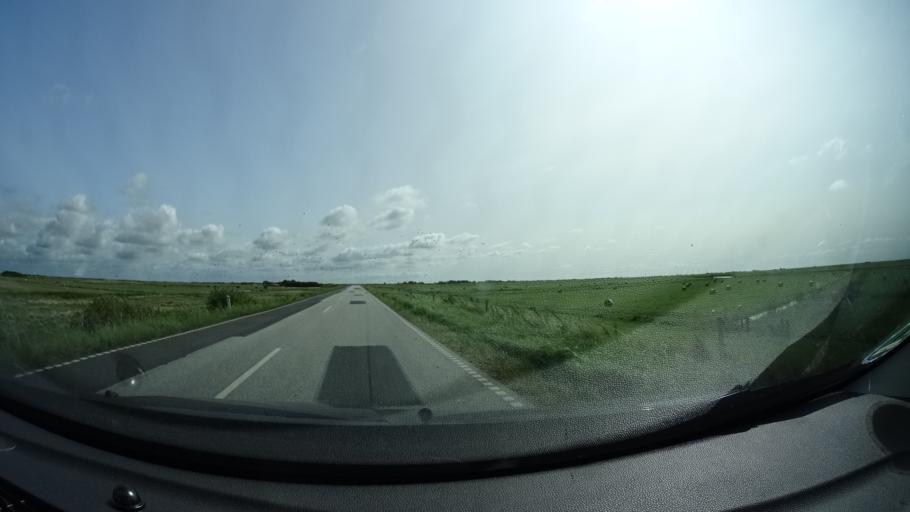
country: DE
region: Schleswig-Holstein
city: Rodenas
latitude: 54.9430
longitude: 8.7095
